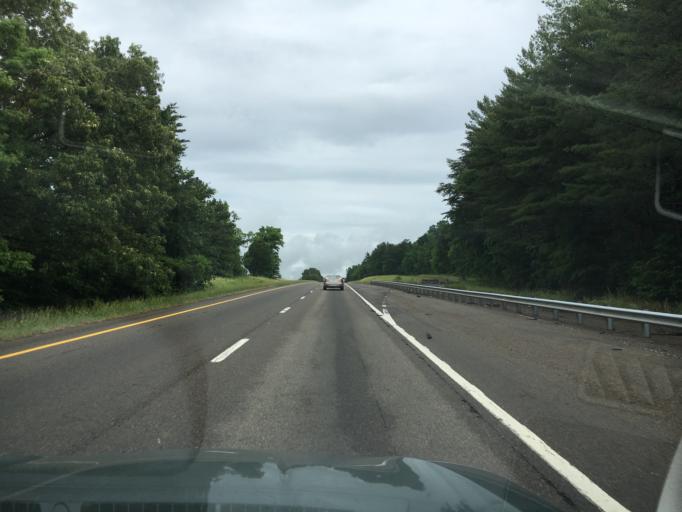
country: US
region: Tennessee
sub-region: Cocke County
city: Newport
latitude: 35.8616
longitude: -83.1840
